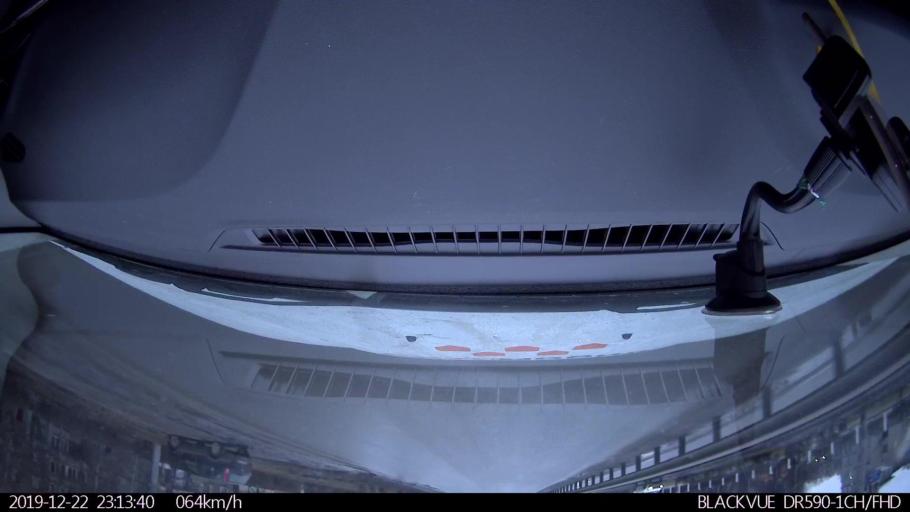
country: RU
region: Nizjnij Novgorod
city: Gorbatovka
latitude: 56.2545
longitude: 43.8527
